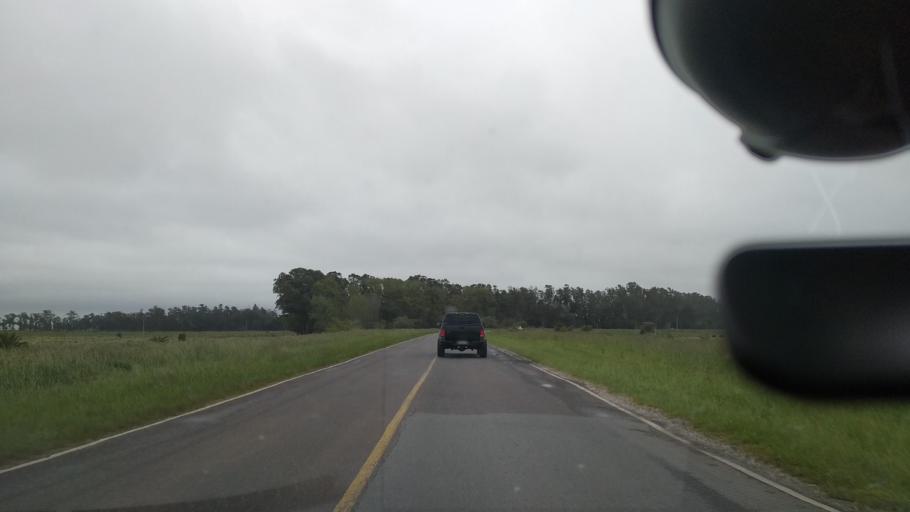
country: AR
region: Buenos Aires
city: Veronica
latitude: -35.5142
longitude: -57.3346
